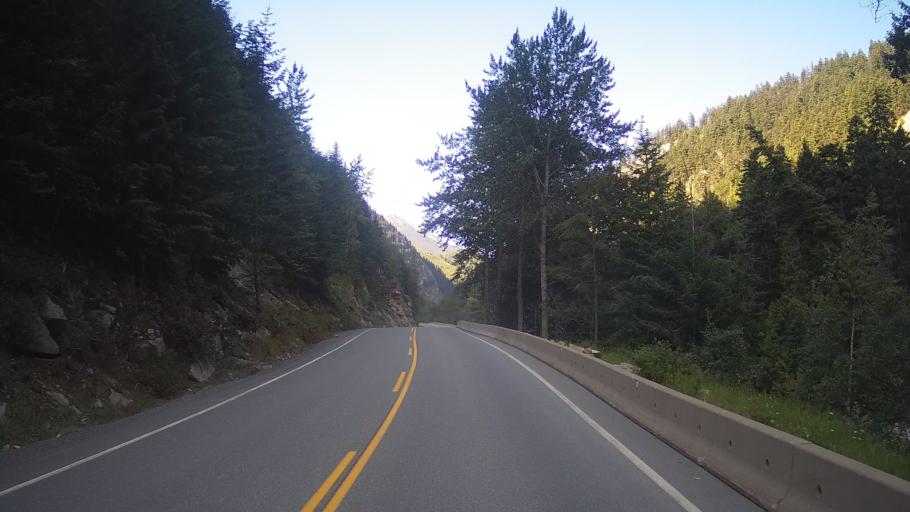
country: CA
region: British Columbia
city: Lillooet
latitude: 50.5503
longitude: -122.1030
